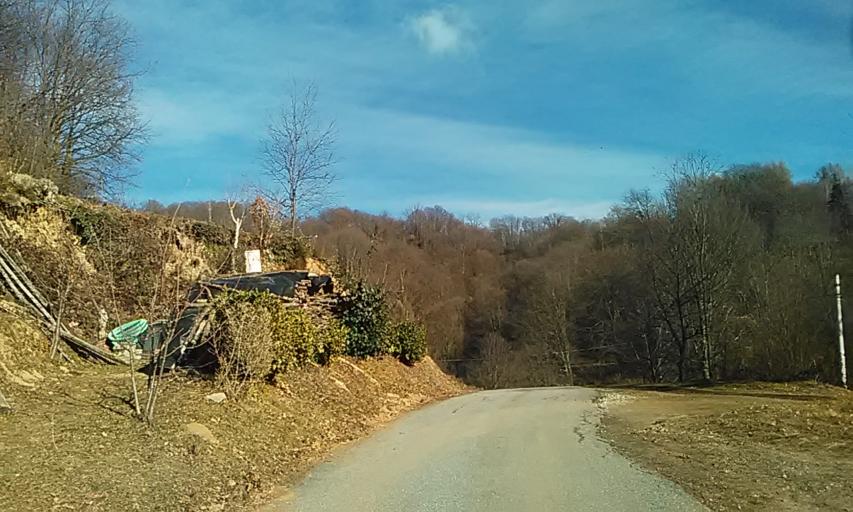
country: IT
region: Piedmont
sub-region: Provincia di Vercelli
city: Cellio
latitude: 45.7370
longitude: 8.3112
